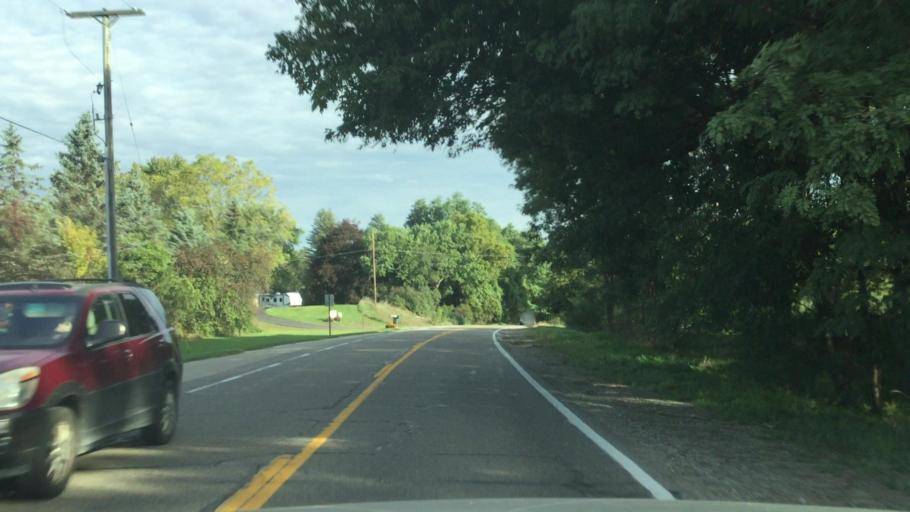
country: US
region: Michigan
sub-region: Livingston County
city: Brighton
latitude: 42.4960
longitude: -83.8596
